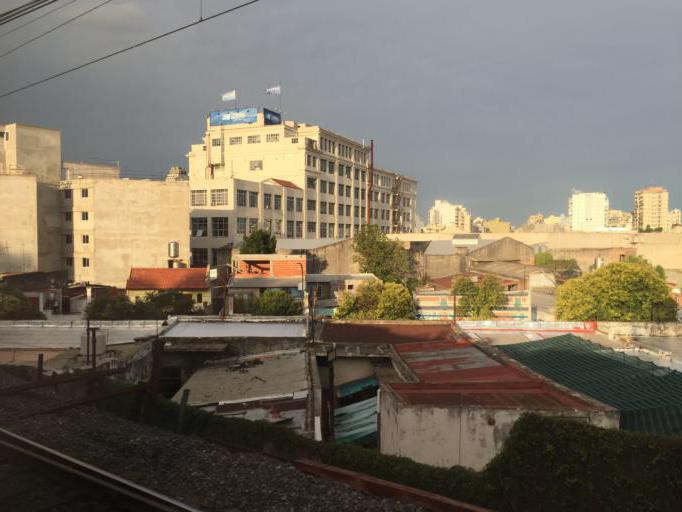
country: AR
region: Buenos Aires
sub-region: Partido de Avellaneda
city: Avellaneda
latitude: -34.6400
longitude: -58.3806
